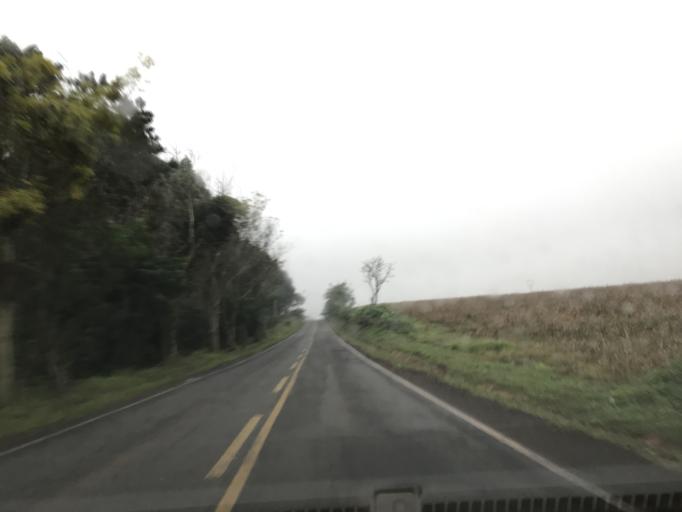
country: PY
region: Canindeyu
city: Salto del Guaira
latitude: -24.0985
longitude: -54.1005
